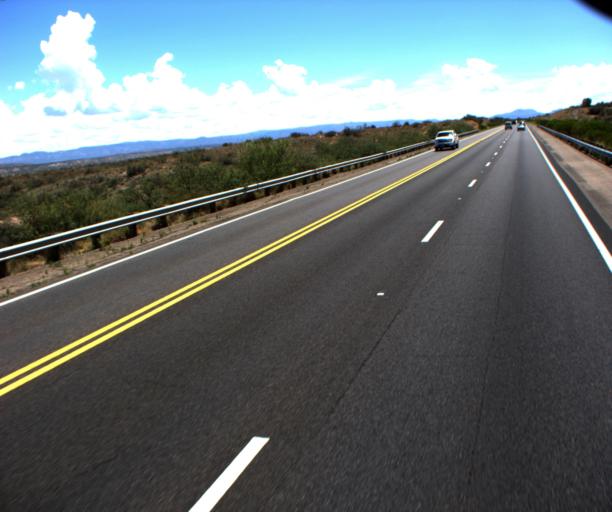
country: US
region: Arizona
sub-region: Yavapai County
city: Cornville
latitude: 34.6328
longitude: -111.9381
